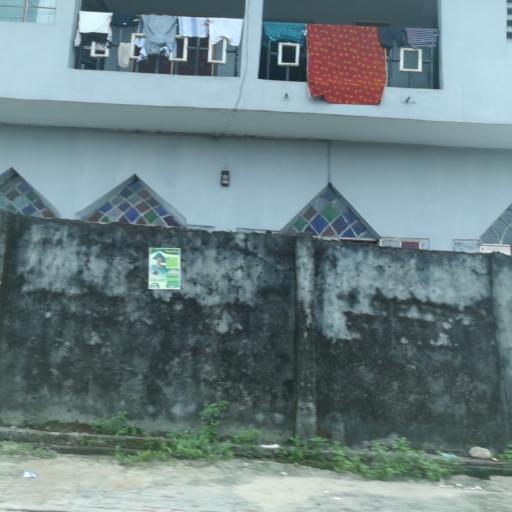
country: NG
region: Rivers
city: Port Harcourt
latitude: 4.7951
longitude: 7.0233
